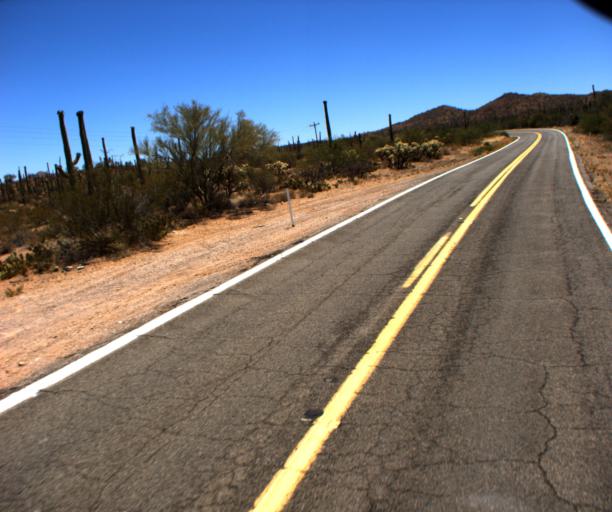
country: US
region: Arizona
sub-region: Pima County
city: Sells
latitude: 32.1729
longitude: -112.2077
